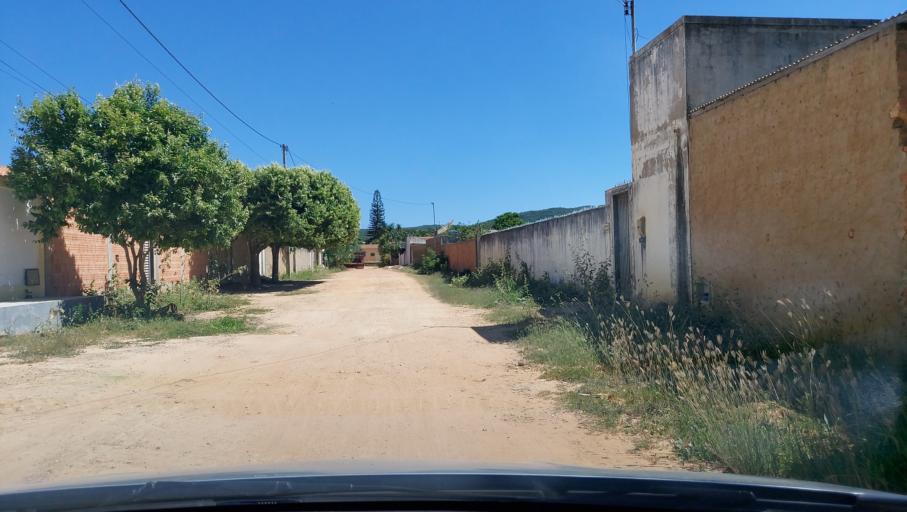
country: BR
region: Bahia
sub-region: Oliveira Dos Brejinhos
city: Beira Rio
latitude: -12.0054
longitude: -42.6271
